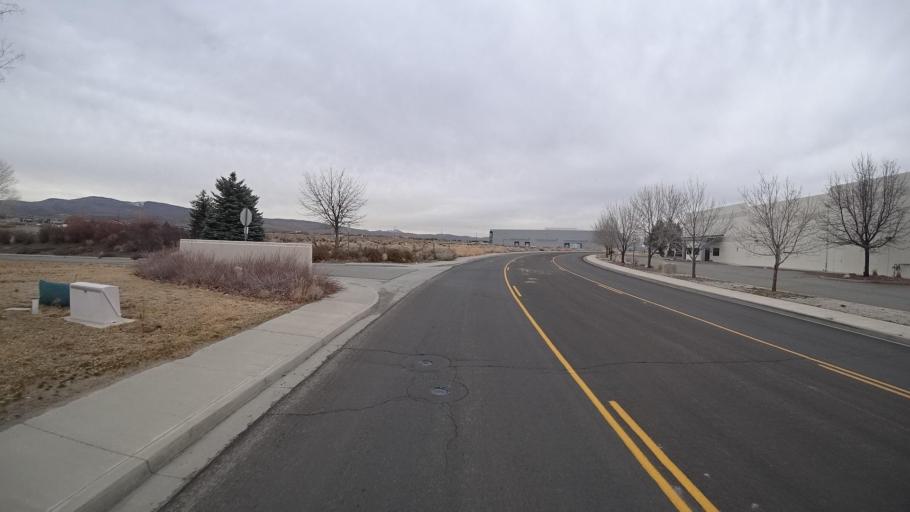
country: US
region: Nevada
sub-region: Washoe County
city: Spanish Springs
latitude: 39.6714
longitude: -119.7043
